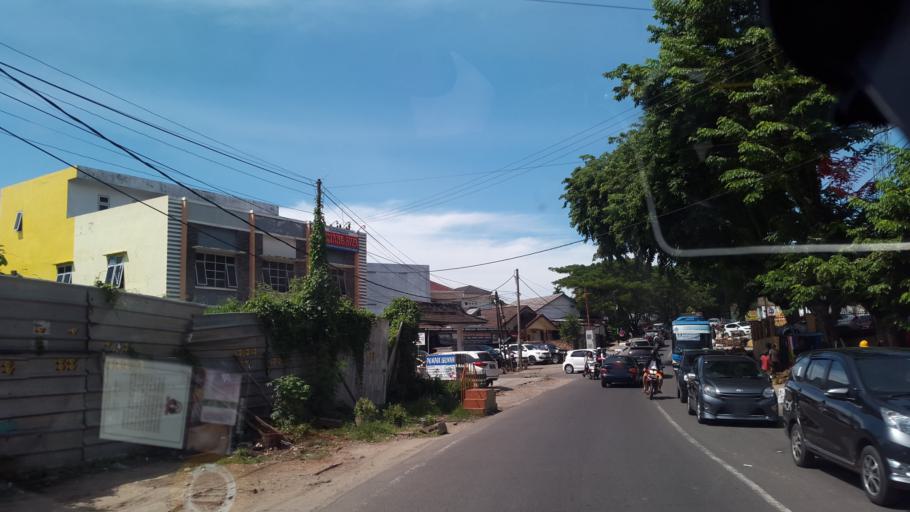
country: ID
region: South Sumatra
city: Plaju
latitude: -2.9895
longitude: 104.7379
